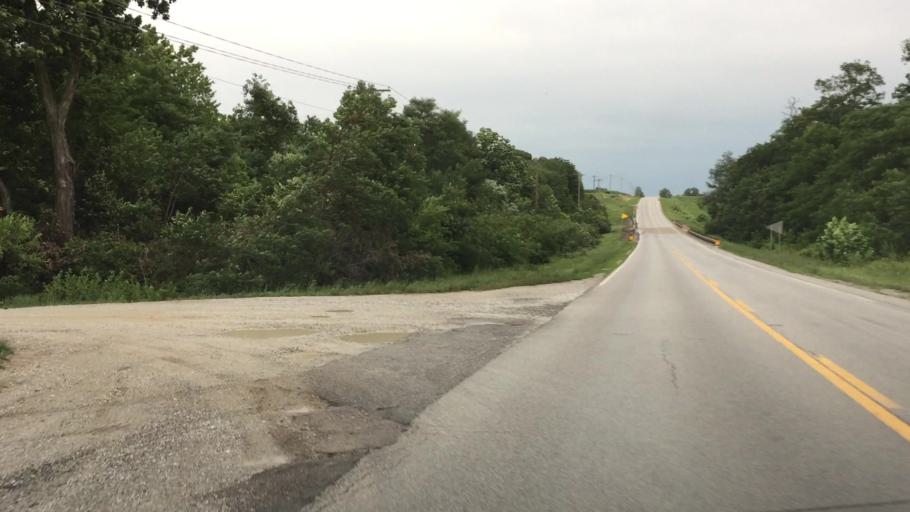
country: US
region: Illinois
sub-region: Hancock County
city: Hamilton
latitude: 40.3612
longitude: -91.3614
